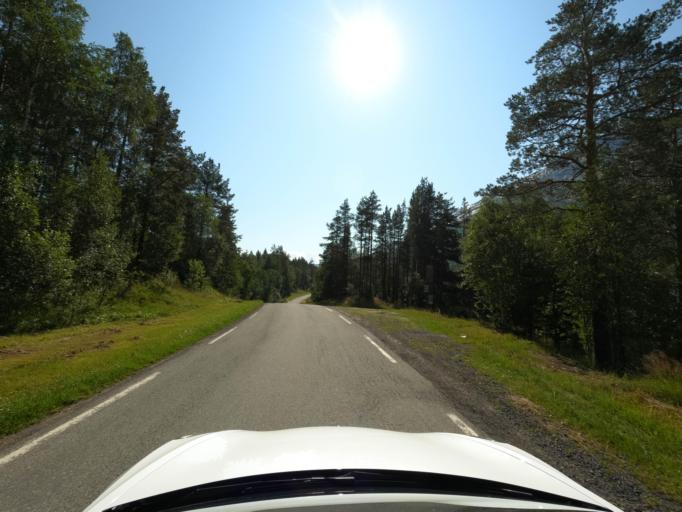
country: NO
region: Nordland
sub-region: Narvik
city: Narvik
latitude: 68.1943
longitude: 17.5563
